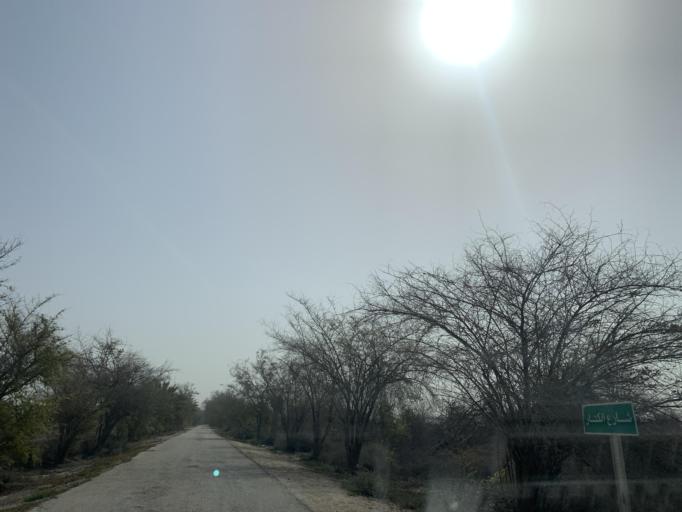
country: BH
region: Northern
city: Madinat `Isa
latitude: 26.1630
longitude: 50.5313
